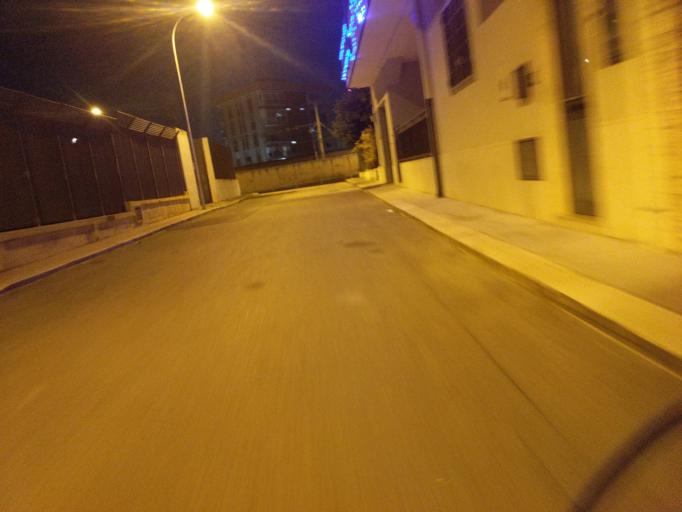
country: IT
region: Apulia
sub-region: Provincia di Bari
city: Modugno
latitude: 41.0877
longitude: 16.7827
